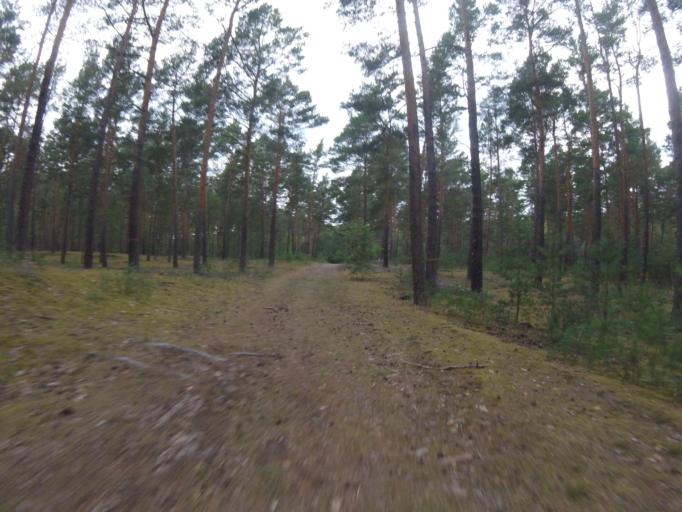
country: DE
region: Brandenburg
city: Gross Koris
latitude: 52.1613
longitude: 13.6745
